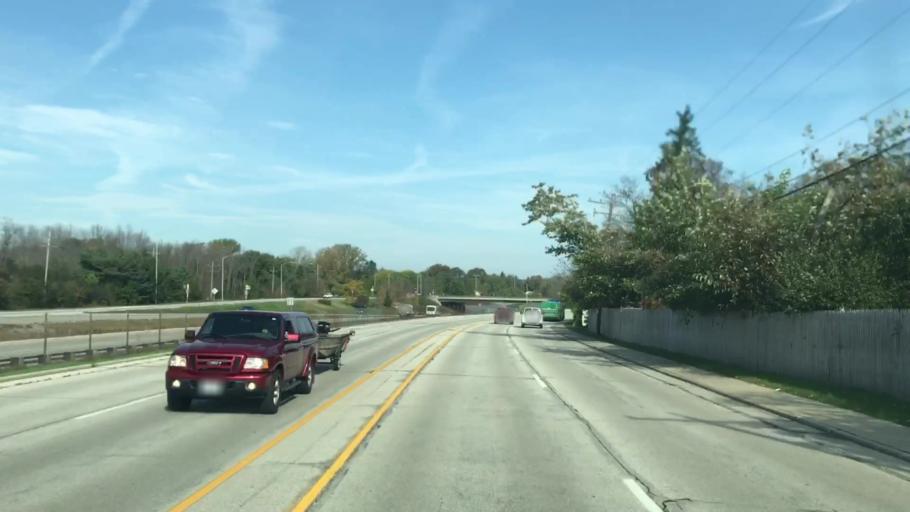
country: US
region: Wisconsin
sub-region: Milwaukee County
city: River Hills
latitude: 43.1892
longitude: -87.9232
